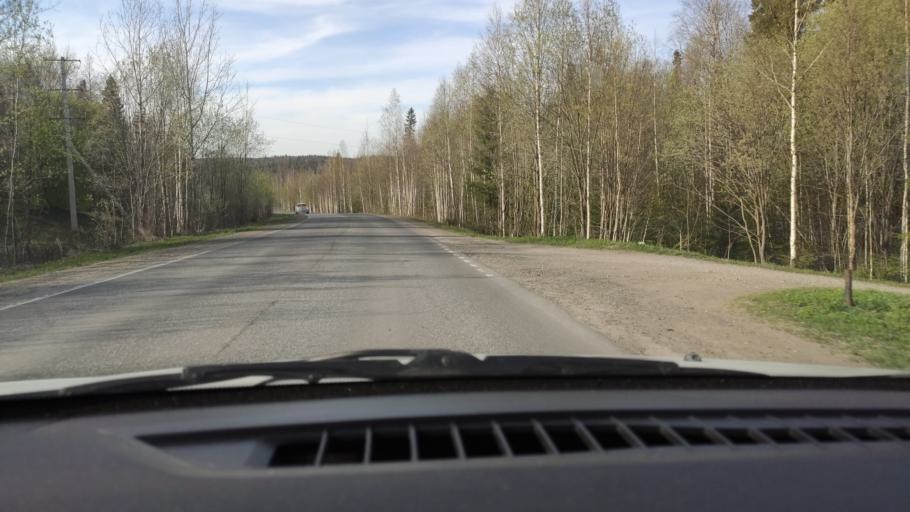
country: RU
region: Perm
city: Novyye Lyady
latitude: 57.9512
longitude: 56.5690
